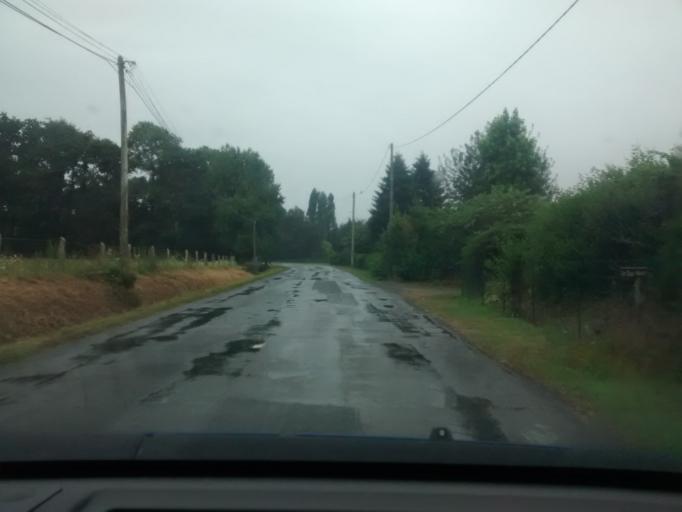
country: FR
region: Brittany
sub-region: Departement d'Ille-et-Vilaine
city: Betton
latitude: 48.1754
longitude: -1.6229
